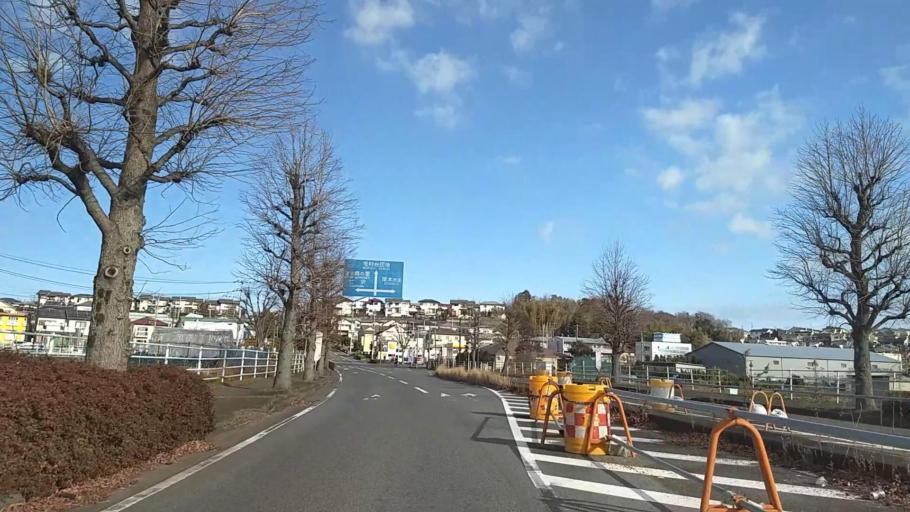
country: JP
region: Kanagawa
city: Atsugi
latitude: 35.4324
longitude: 139.3305
